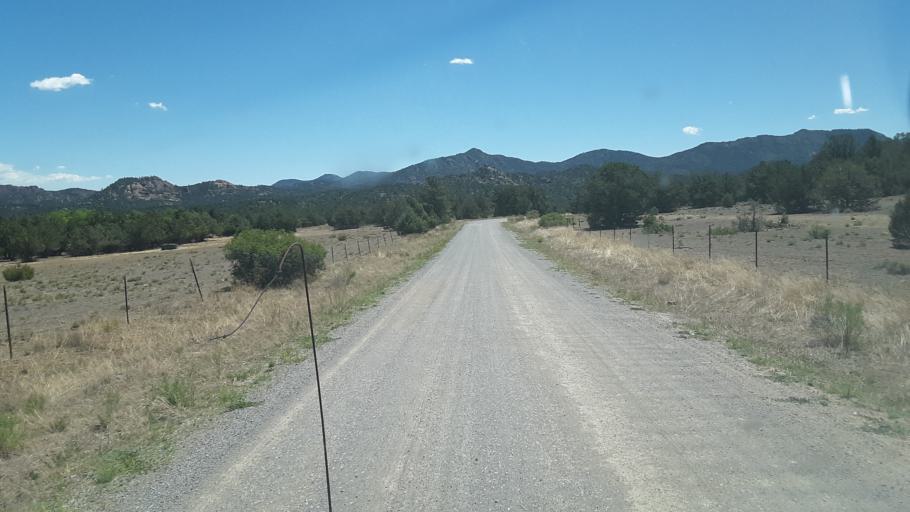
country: US
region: Colorado
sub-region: Custer County
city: Westcliffe
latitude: 38.3055
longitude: -105.6180
